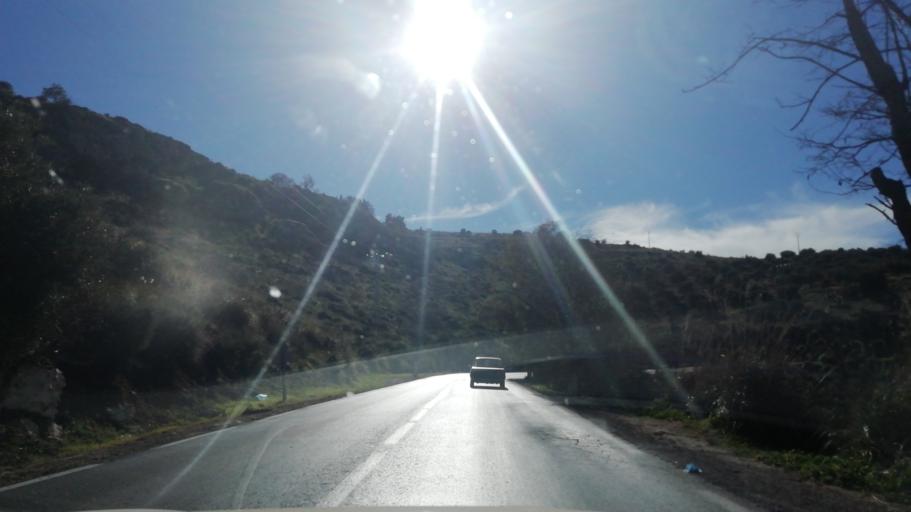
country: DZ
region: Tlemcen
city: Mansoura
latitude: 34.8538
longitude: -1.3477
